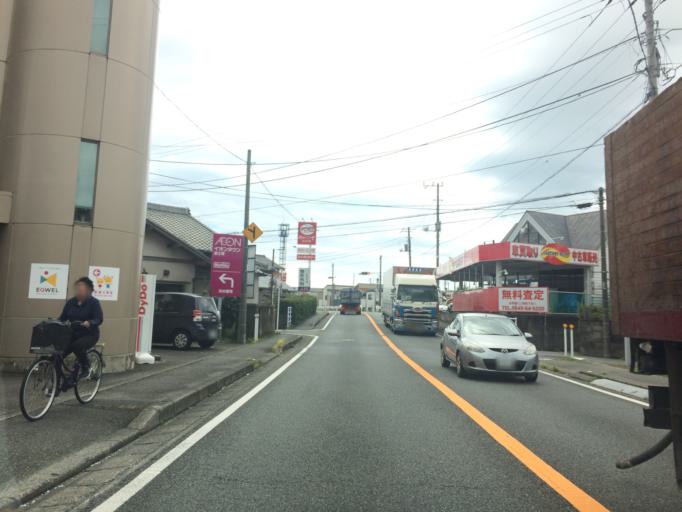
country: JP
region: Shizuoka
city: Fuji
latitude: 35.1453
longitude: 138.6468
